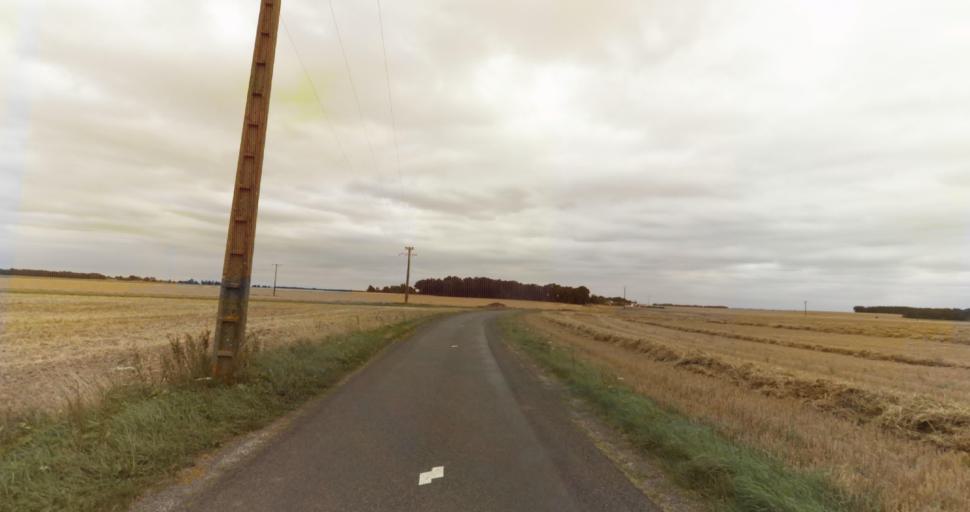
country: FR
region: Haute-Normandie
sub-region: Departement de l'Eure
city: Menilles
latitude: 48.9393
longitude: 1.2689
